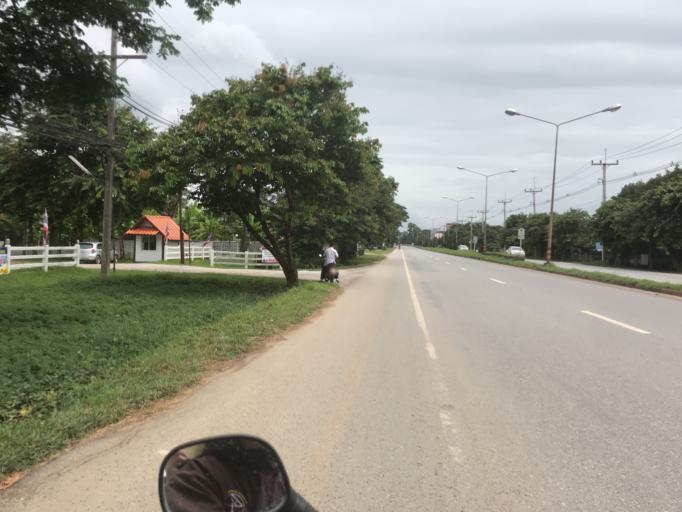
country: TH
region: Chiang Rai
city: Chiang Rai
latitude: 19.9449
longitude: 99.8471
